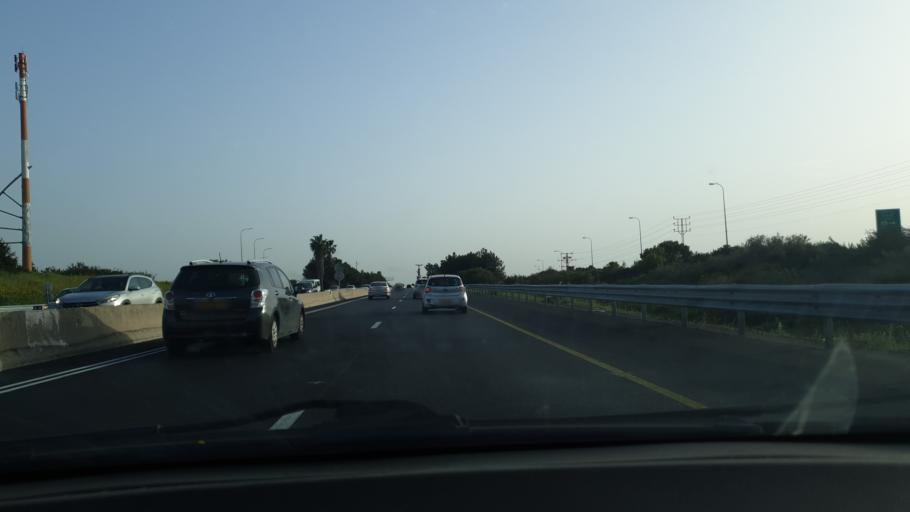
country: IL
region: Central District
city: Even Yehuda
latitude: 32.2381
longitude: 34.8861
